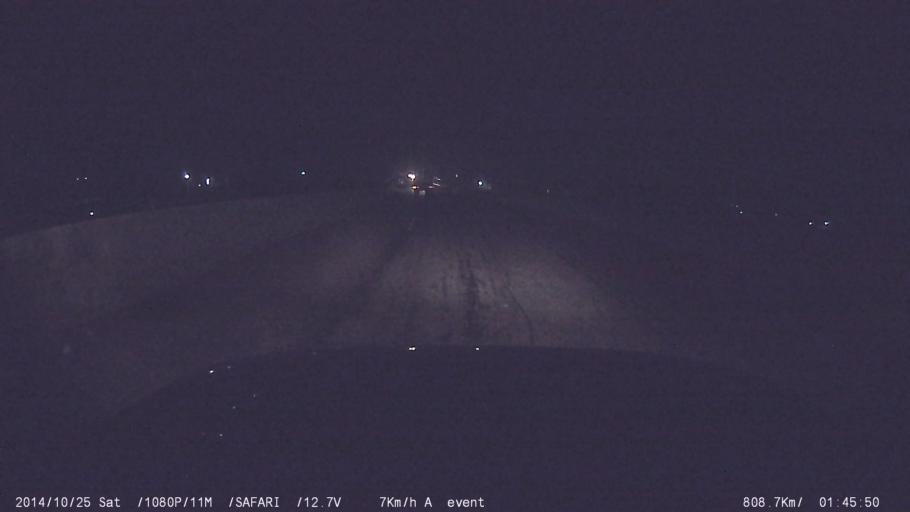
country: IN
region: Tamil Nadu
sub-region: Tiruppur
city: Avinashi
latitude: 11.1532
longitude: 77.2111
